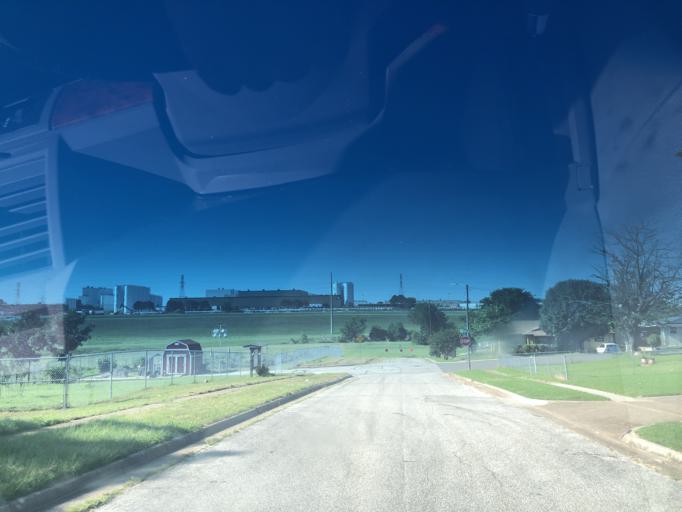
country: US
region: Texas
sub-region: Dallas County
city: Grand Prairie
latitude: 32.7278
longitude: -97.0364
